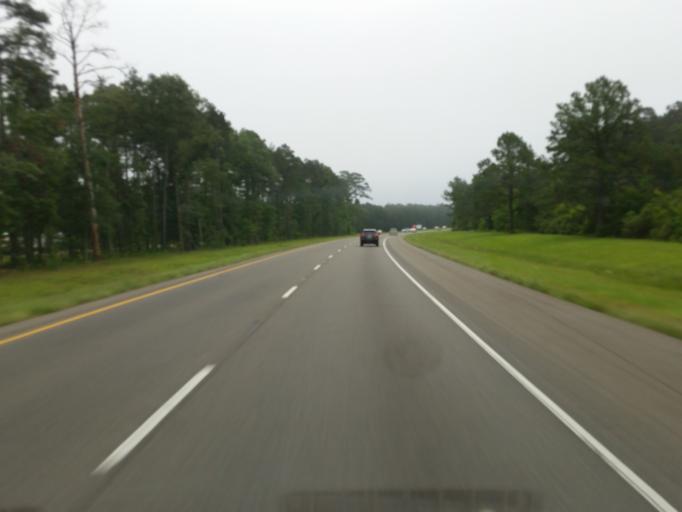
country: US
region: Louisiana
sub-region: Bossier Parish
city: Haughton
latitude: 32.5757
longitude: -93.4776
